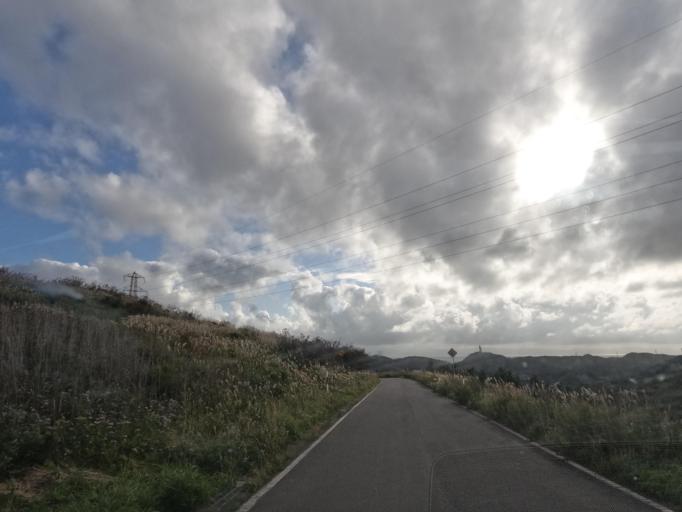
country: JP
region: Hokkaido
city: Muroran
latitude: 42.3157
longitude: 141.0063
